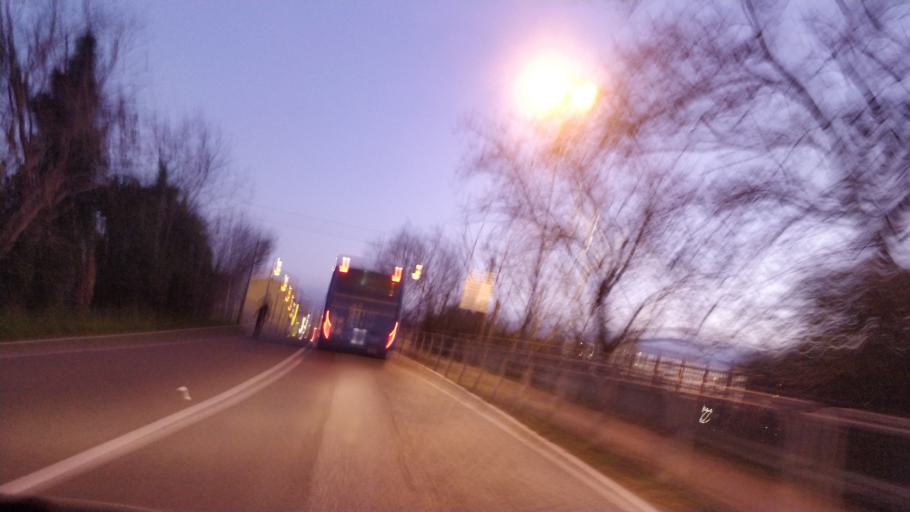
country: IT
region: Tuscany
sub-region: Provincia di Livorno
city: Cecina
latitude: 43.3158
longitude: 10.5138
